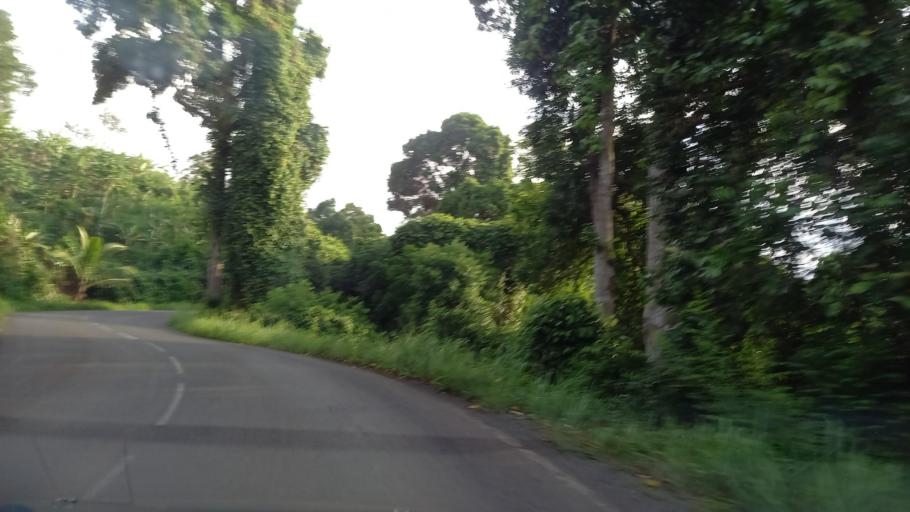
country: YT
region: Bandraboua
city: Bandraboua
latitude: -12.7394
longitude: 45.1179
